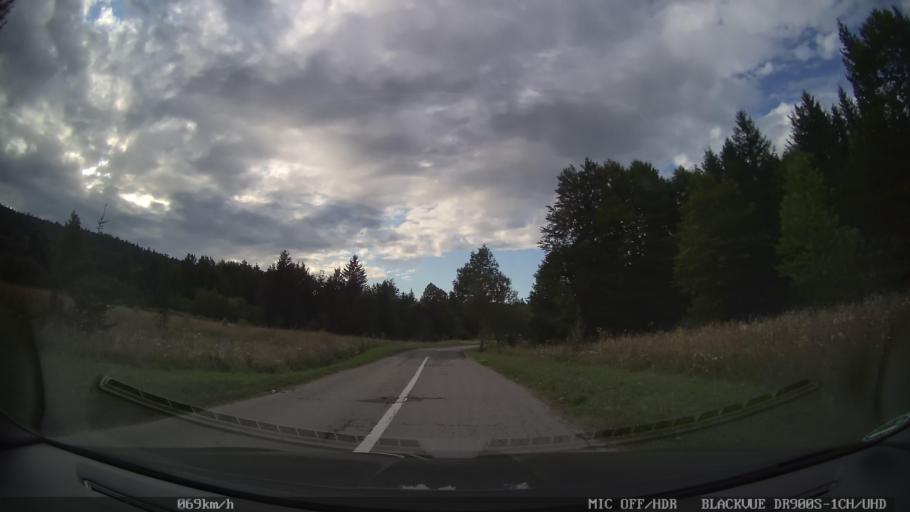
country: HR
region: Licko-Senjska
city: Jezerce
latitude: 44.9572
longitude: 15.5263
